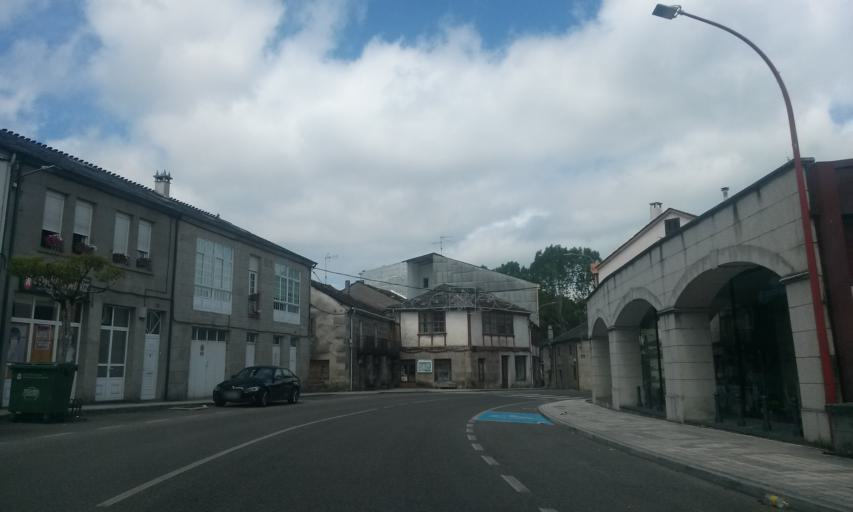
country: ES
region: Galicia
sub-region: Provincia de Lugo
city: Friol
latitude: 43.0299
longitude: -7.7939
